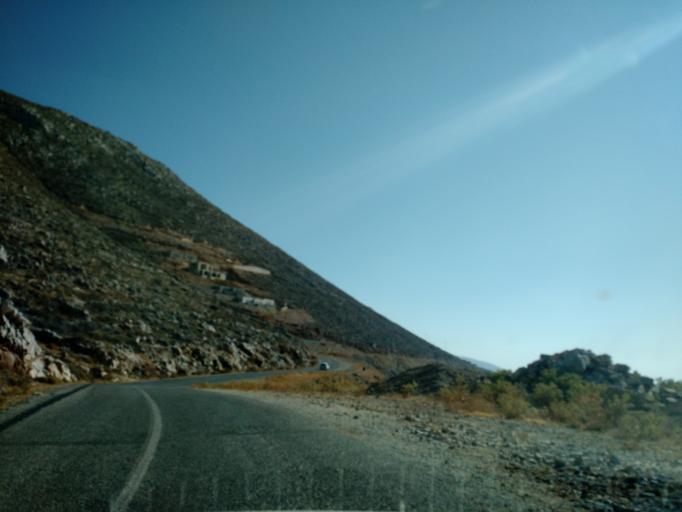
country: GR
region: South Aegean
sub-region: Nomos Kykladon
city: Amorgos
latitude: 36.8939
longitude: 25.9643
